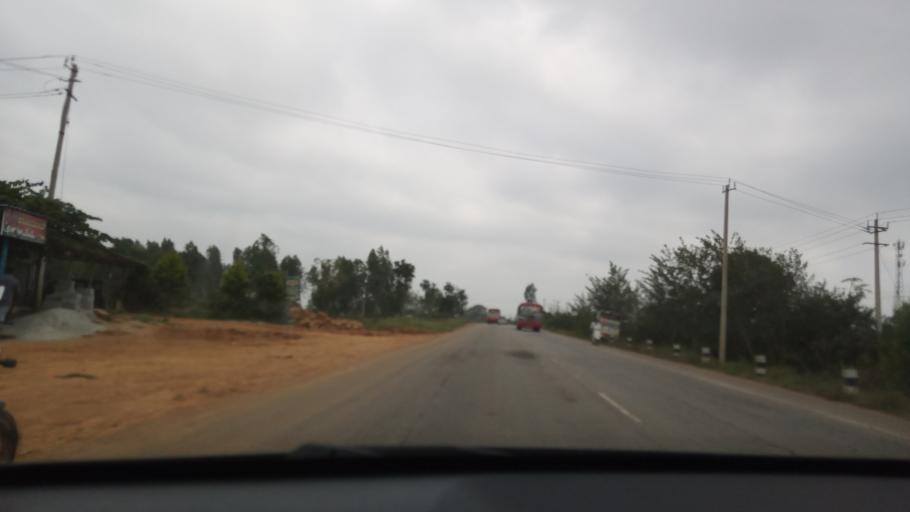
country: IN
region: Karnataka
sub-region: Chikkaballapur
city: Sidlaghatta
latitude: 13.2879
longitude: 77.9618
